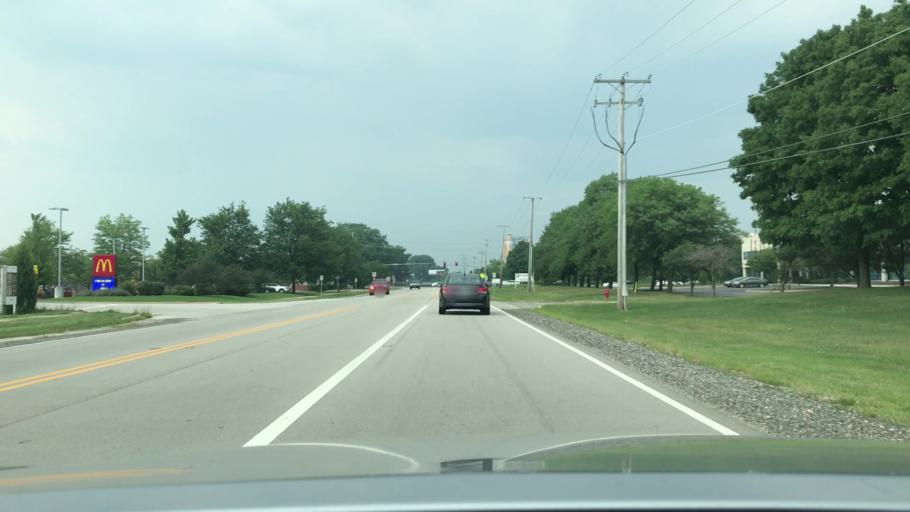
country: US
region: Illinois
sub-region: Will County
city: Plainfield
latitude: 41.6346
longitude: -88.2223
